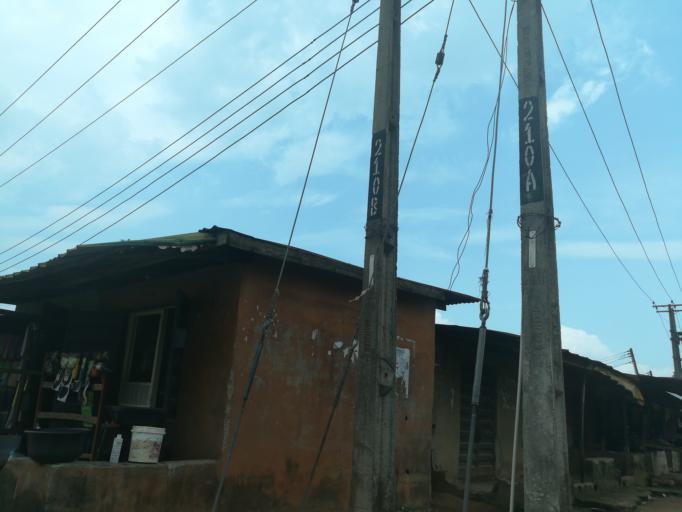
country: NG
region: Lagos
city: Ikorodu
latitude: 6.5639
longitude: 3.5972
